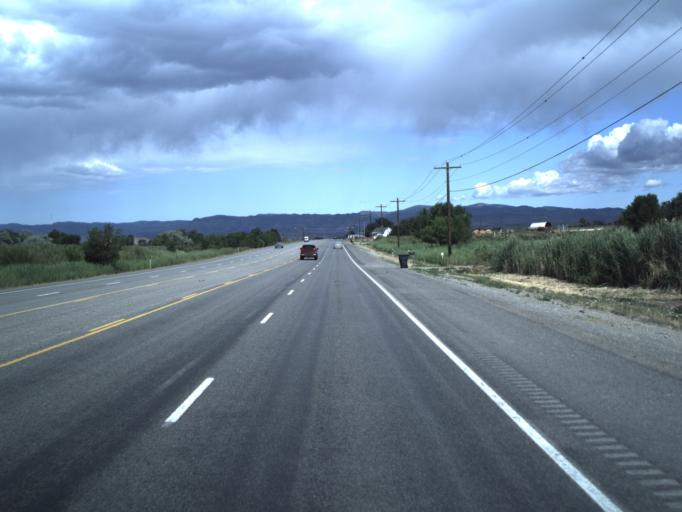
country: US
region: Utah
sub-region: Carbon County
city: Wellington
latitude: 39.5551
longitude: -110.7593
